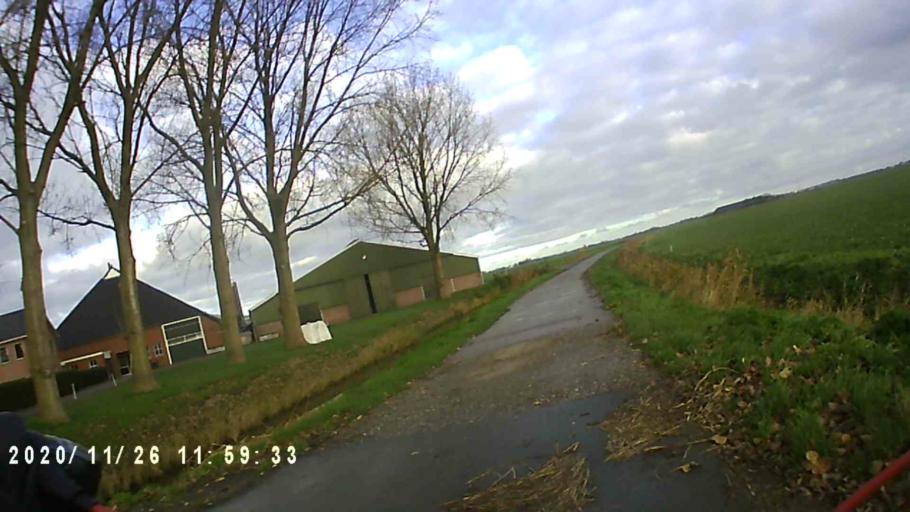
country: NL
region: Groningen
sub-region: Gemeente Bedum
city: Bedum
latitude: 53.3164
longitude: 6.6043
